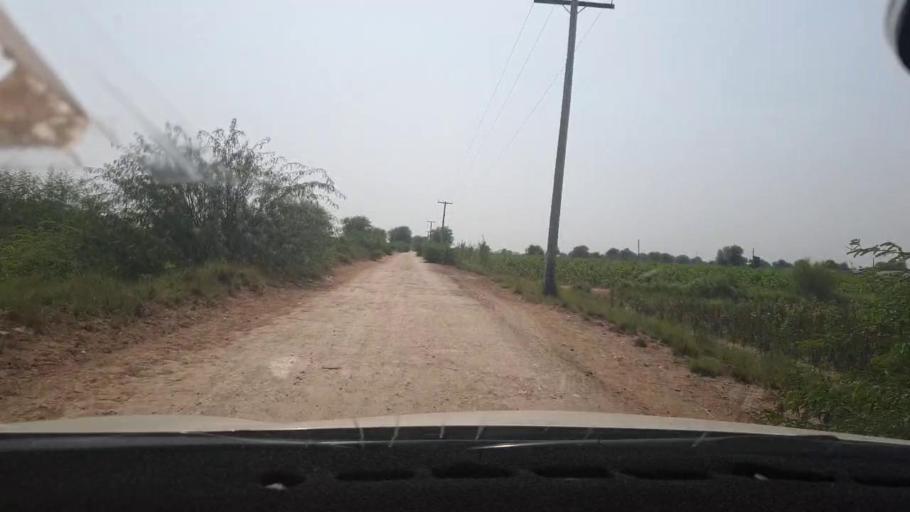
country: PK
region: Sindh
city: Tando Mittha Khan
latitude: 25.9382
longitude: 69.2247
